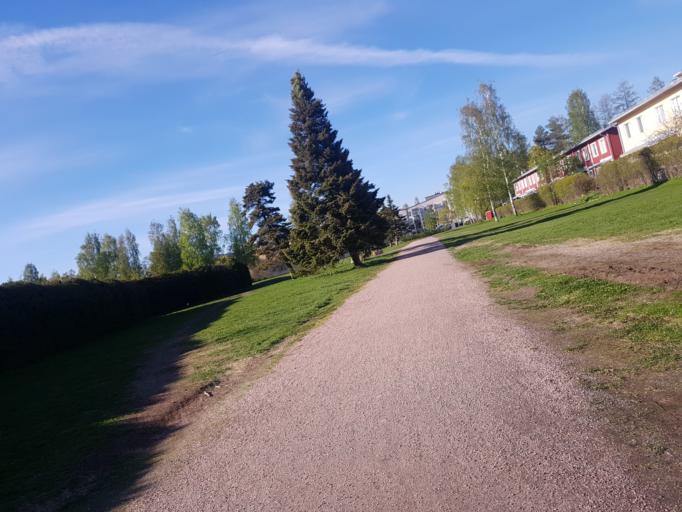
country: FI
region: Uusimaa
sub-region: Helsinki
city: Vantaa
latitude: 60.2723
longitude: 25.0302
